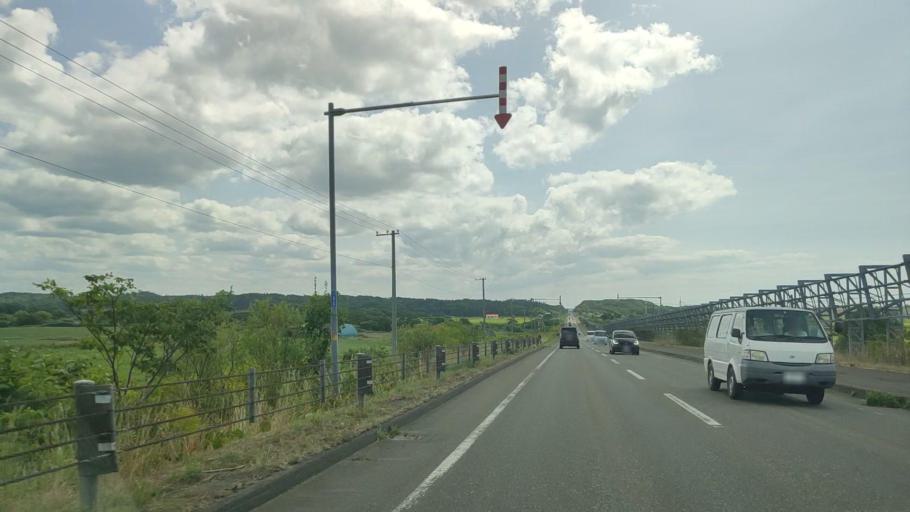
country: JP
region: Hokkaido
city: Makubetsu
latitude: 44.7774
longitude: 141.7915
